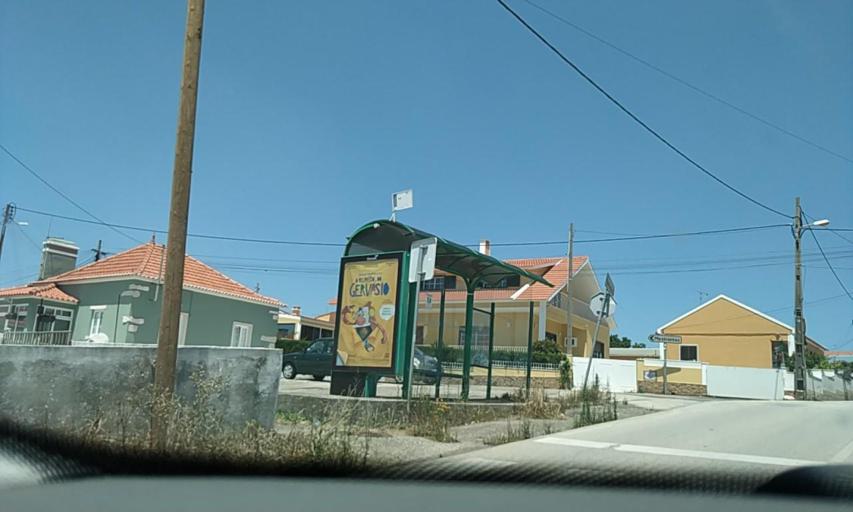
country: PT
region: Lisbon
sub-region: Sintra
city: Almargem
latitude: 38.8771
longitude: -9.2808
